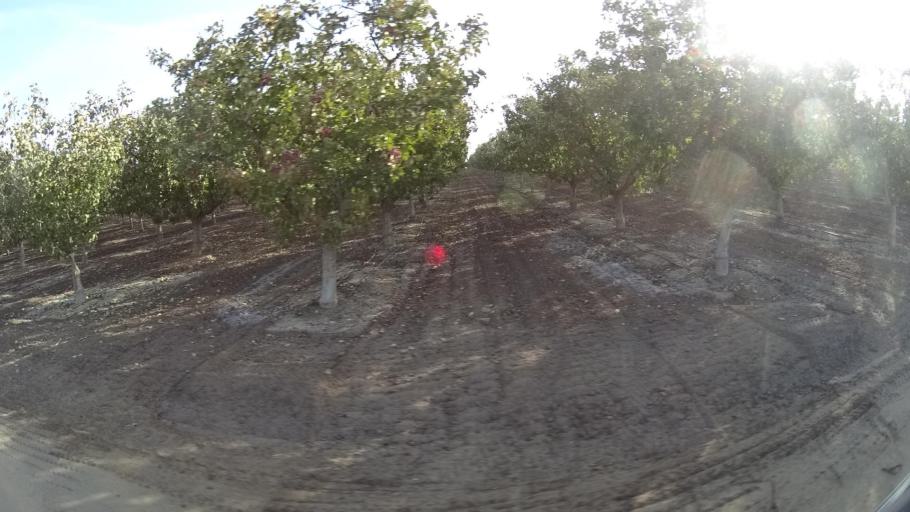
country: US
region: California
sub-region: Kern County
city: McFarland
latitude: 35.7315
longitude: -119.1872
